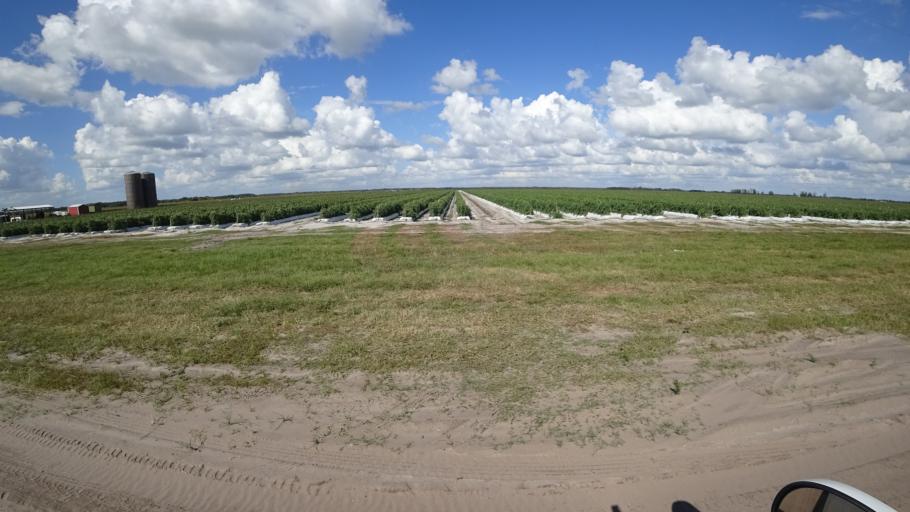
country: US
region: Florida
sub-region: DeSoto County
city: Arcadia
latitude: 27.3244
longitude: -82.0957
